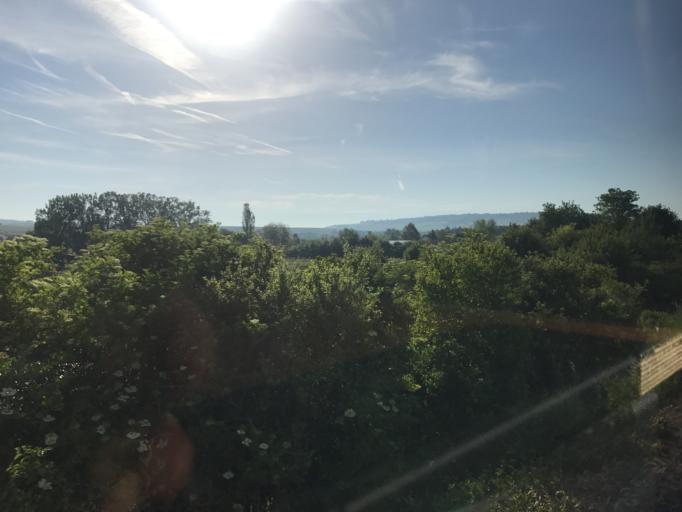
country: DE
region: Rheinland-Pfalz
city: Zotzenheim
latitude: 49.8655
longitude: 7.9735
